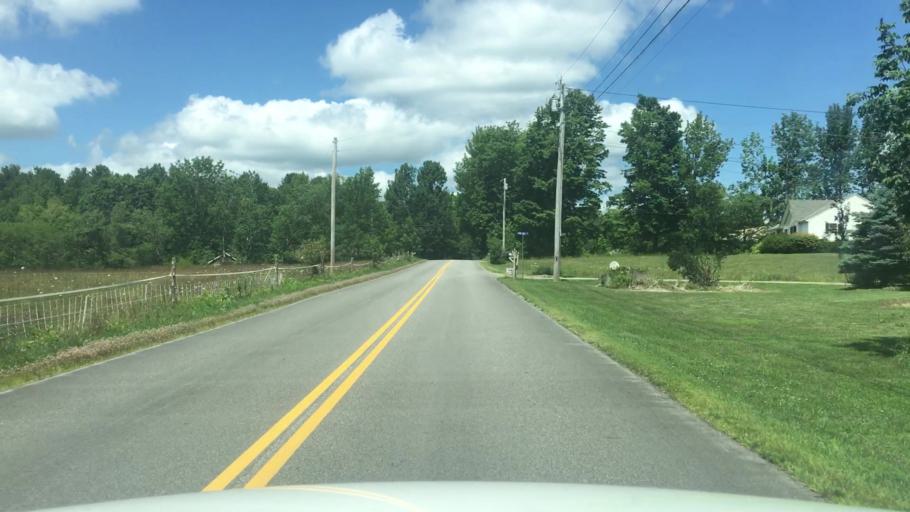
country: US
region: Maine
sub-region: Waldo County
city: Belfast
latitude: 44.4126
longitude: -69.0386
